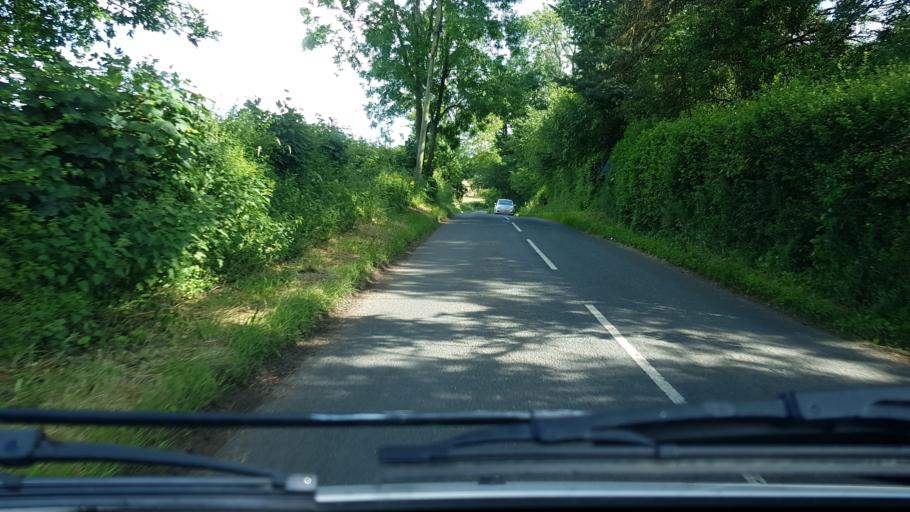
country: GB
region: England
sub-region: Worcestershire
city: Bewdley
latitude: 52.4084
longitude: -2.3096
